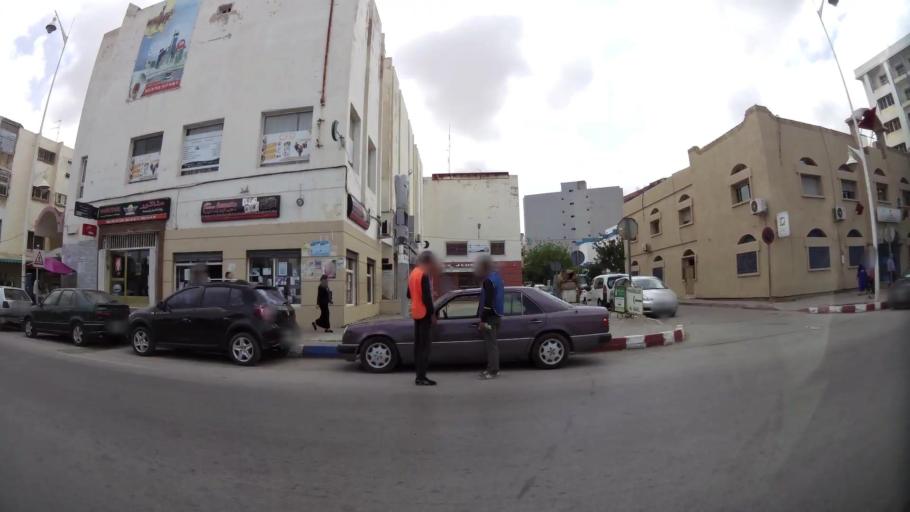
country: MA
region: Oriental
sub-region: Nador
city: Nador
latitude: 35.1759
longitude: -2.9263
